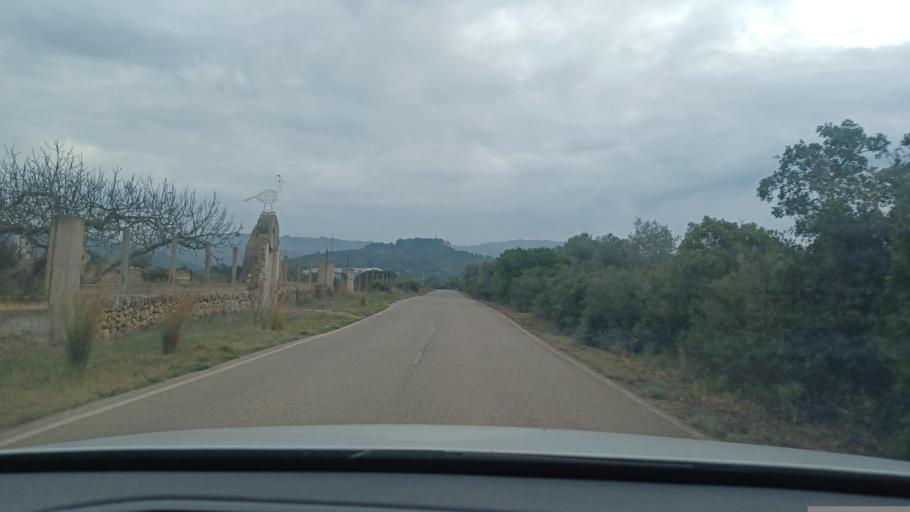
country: ES
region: Catalonia
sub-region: Provincia de Tarragona
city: Santa Barbara
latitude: 40.6629
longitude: 0.4585
